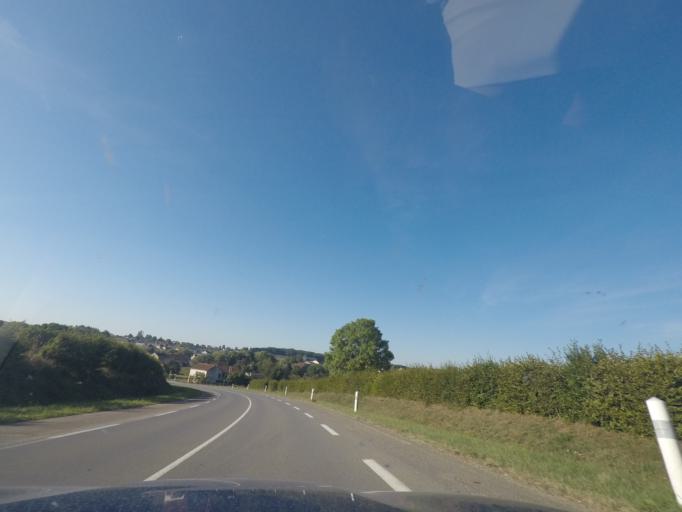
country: LU
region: Luxembourg
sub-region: Canton d'Esch-sur-Alzette
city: Frisange
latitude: 49.4608
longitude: 6.1782
